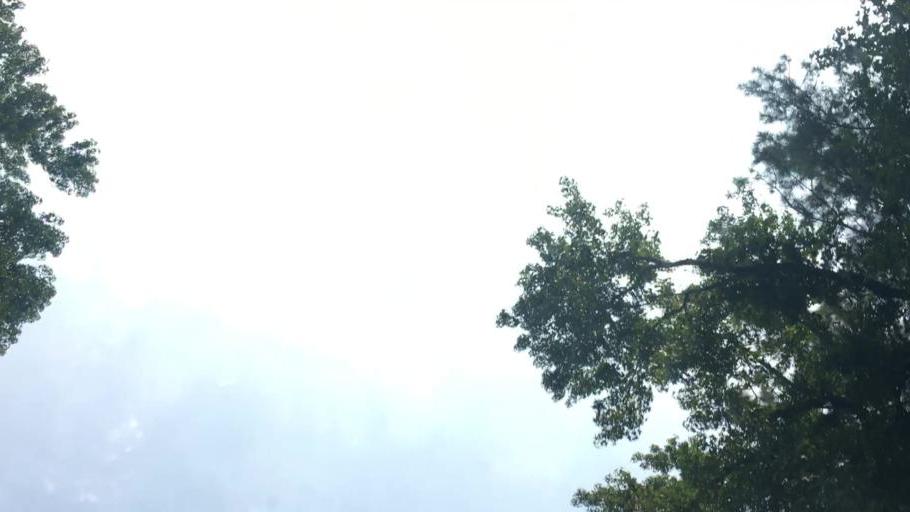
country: US
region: Alabama
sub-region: Bibb County
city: Woodstock
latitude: 33.2182
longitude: -87.1103
